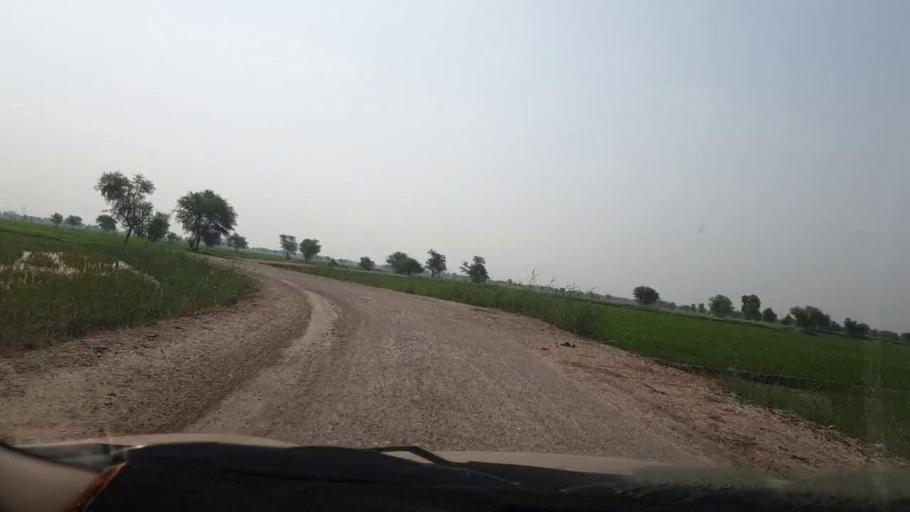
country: PK
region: Sindh
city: Goth Garelo
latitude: 27.4453
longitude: 68.0367
